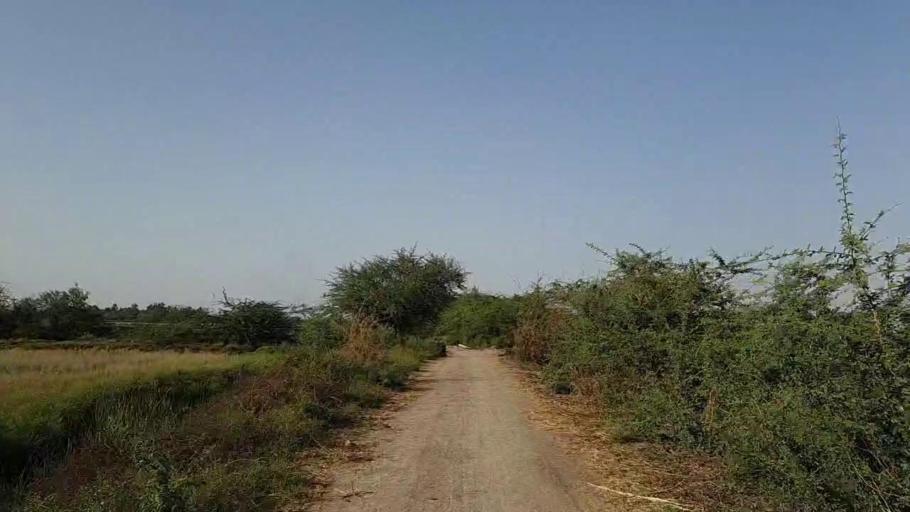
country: PK
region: Sindh
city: Jati
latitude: 24.2901
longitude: 68.1491
